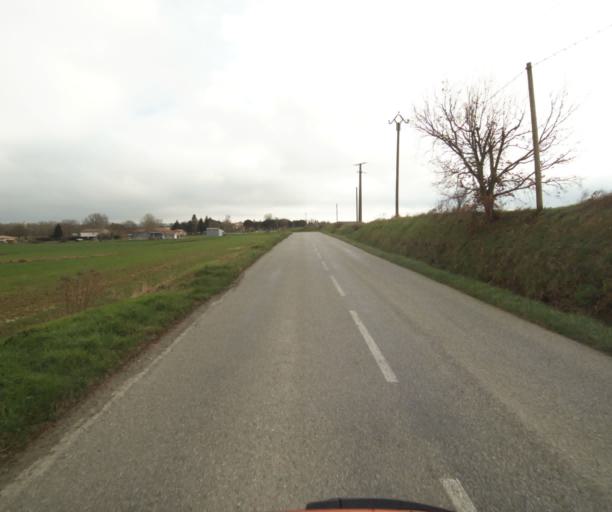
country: FR
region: Languedoc-Roussillon
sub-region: Departement de l'Aude
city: Belpech
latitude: 43.2045
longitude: 1.7318
